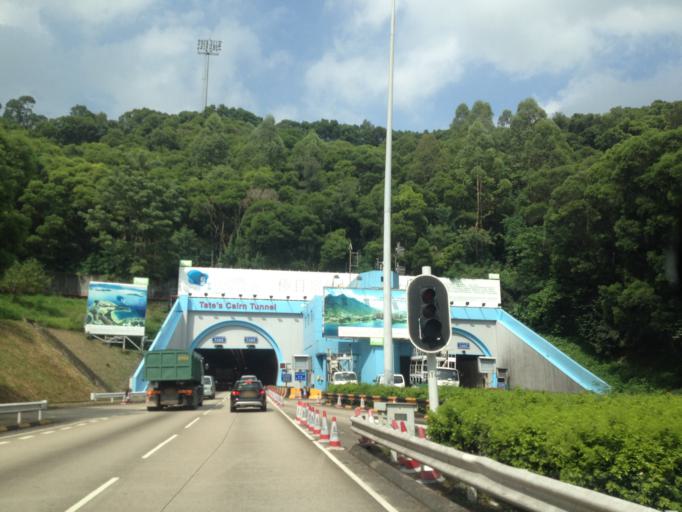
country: HK
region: Wong Tai Sin
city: Wong Tai Sin
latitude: 22.3413
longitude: 114.2041
